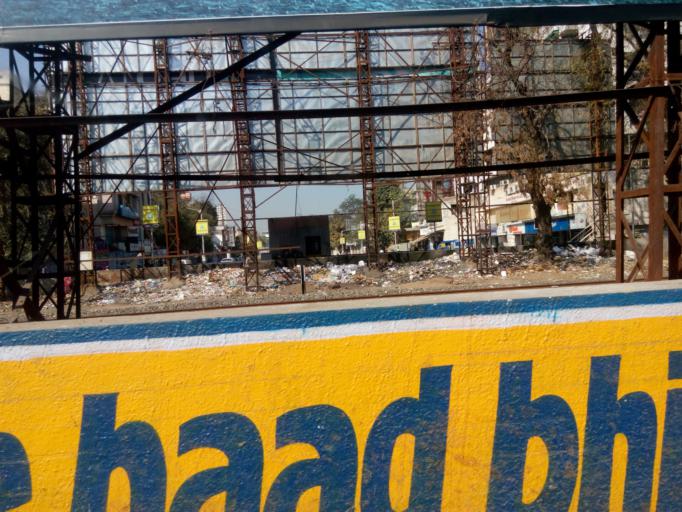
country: IN
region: Gujarat
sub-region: Ahmadabad
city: Ahmedabad
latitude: 23.0354
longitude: 72.5657
